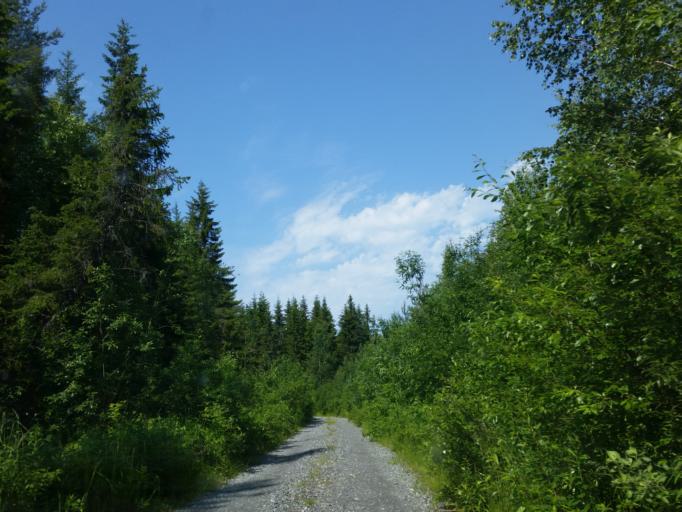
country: FI
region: Northern Savo
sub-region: Ylae-Savo
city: Keitele
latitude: 63.1039
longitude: 26.5407
